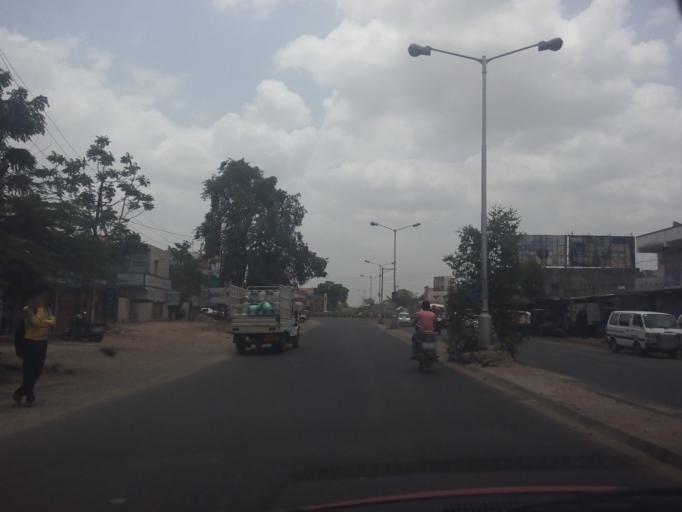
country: IN
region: Gujarat
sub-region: Ahmadabad
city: Sarkhej
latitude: 22.9871
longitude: 72.4934
